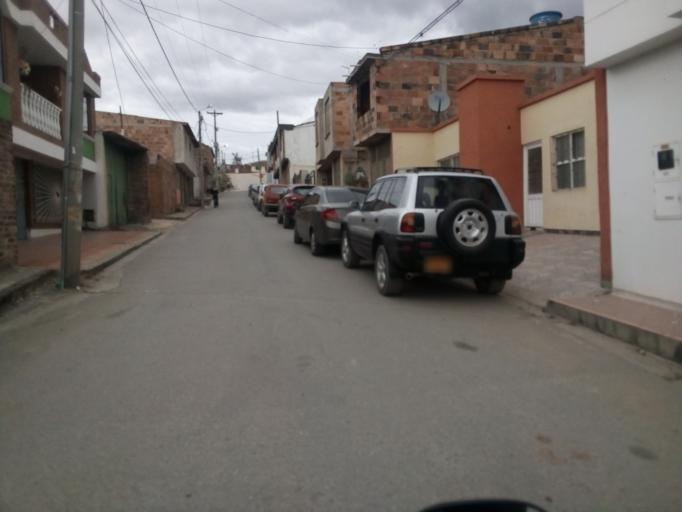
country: CO
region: Boyaca
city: Toca
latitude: 5.5647
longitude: -73.1831
